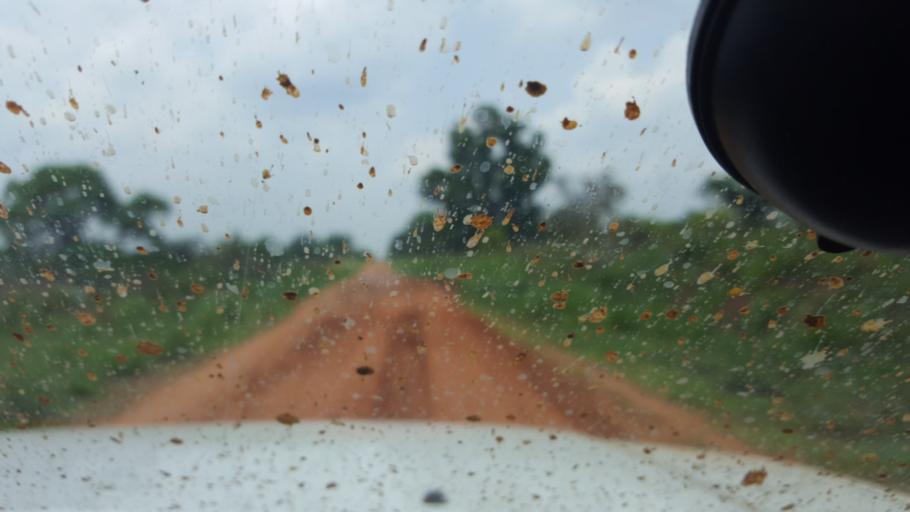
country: CD
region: Bandundu
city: Bandundu
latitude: -3.7008
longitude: 16.8524
